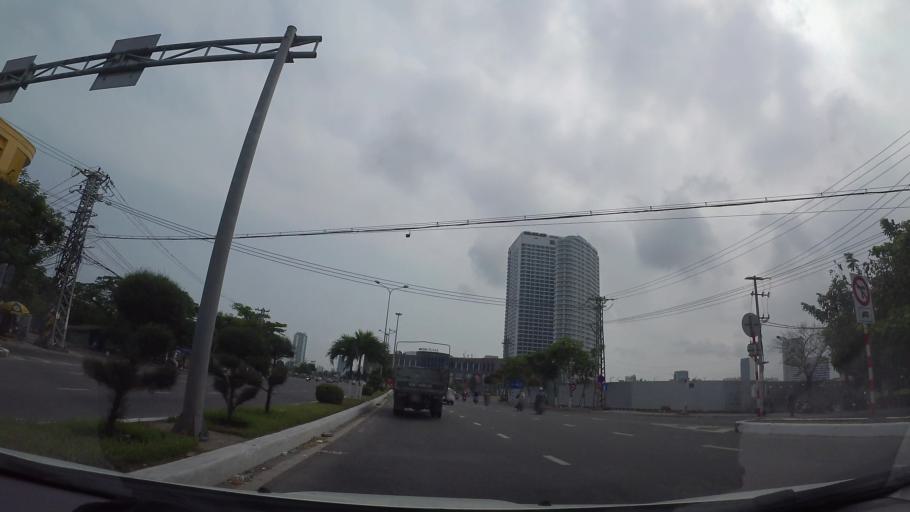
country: VN
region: Da Nang
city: Da Nang
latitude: 16.0741
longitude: 108.2304
